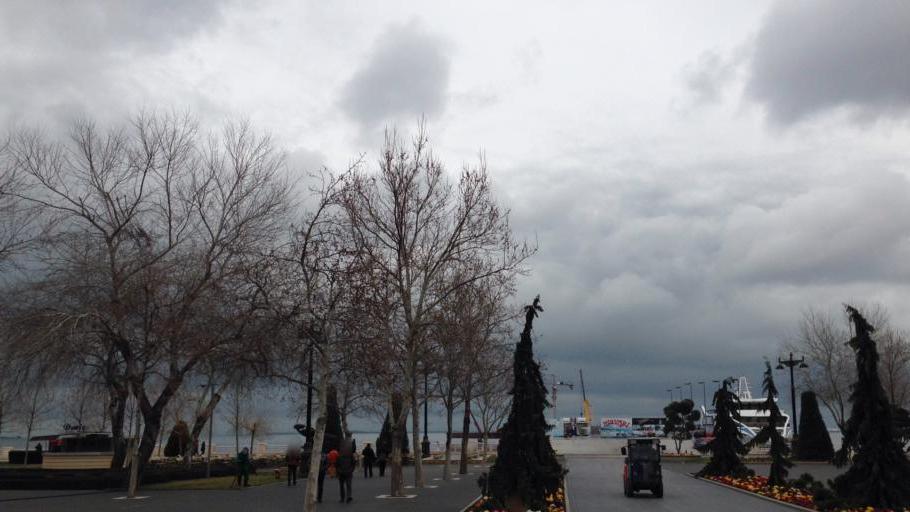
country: AZ
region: Baki
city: Baku
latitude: 40.3702
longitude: 49.8492
